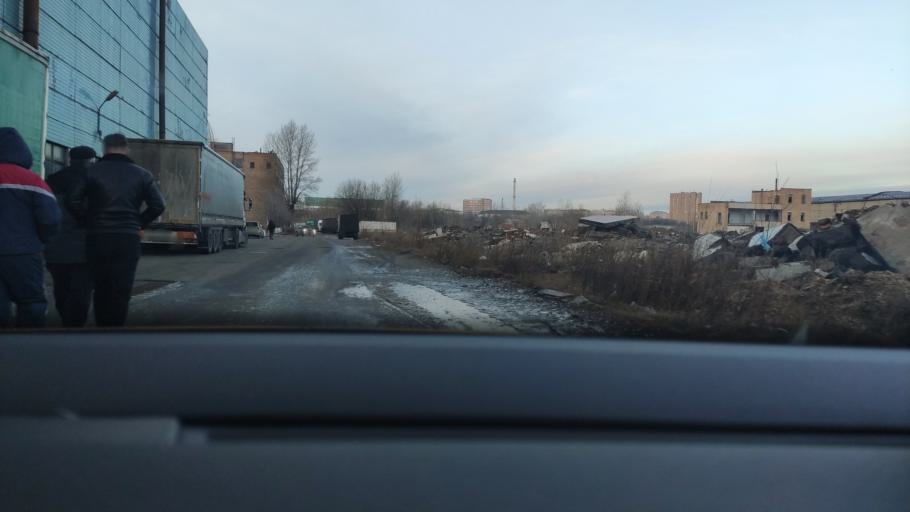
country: RU
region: Moskovskaya
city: Kozhukhovo
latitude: 55.6894
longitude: 37.6411
